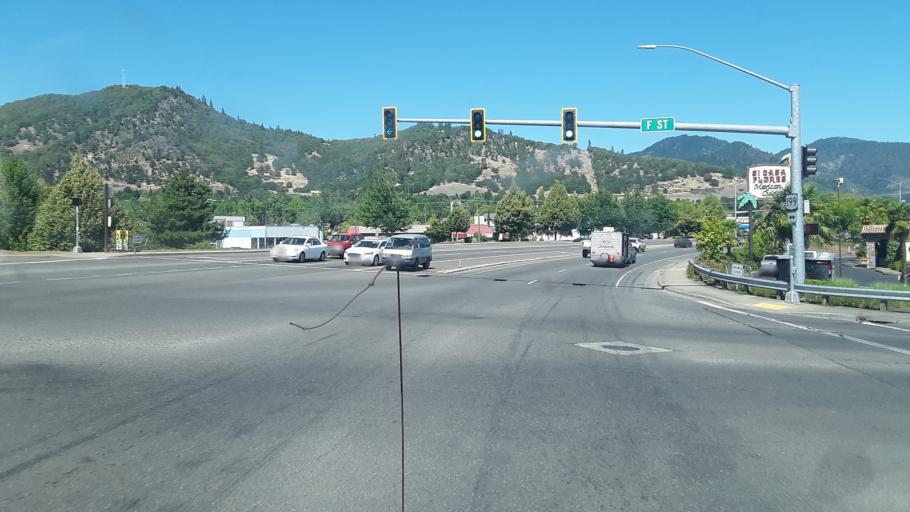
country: US
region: Oregon
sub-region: Josephine County
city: Fruitdale
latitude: 42.4368
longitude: -123.3106
